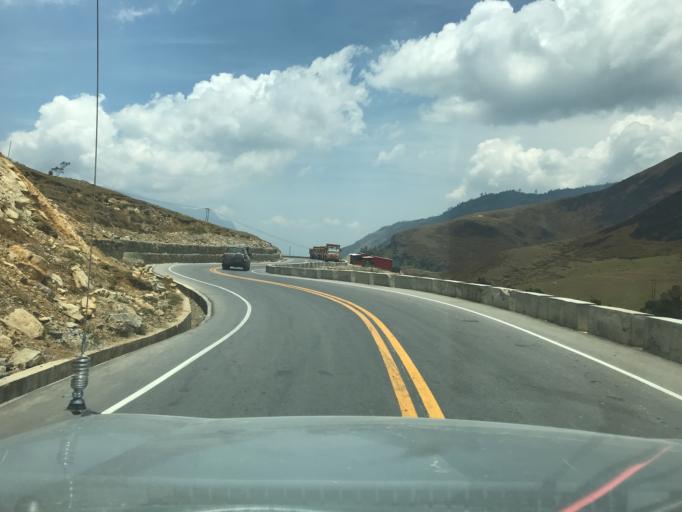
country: TL
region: Manufahi
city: Same
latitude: -8.8786
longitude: 125.6049
